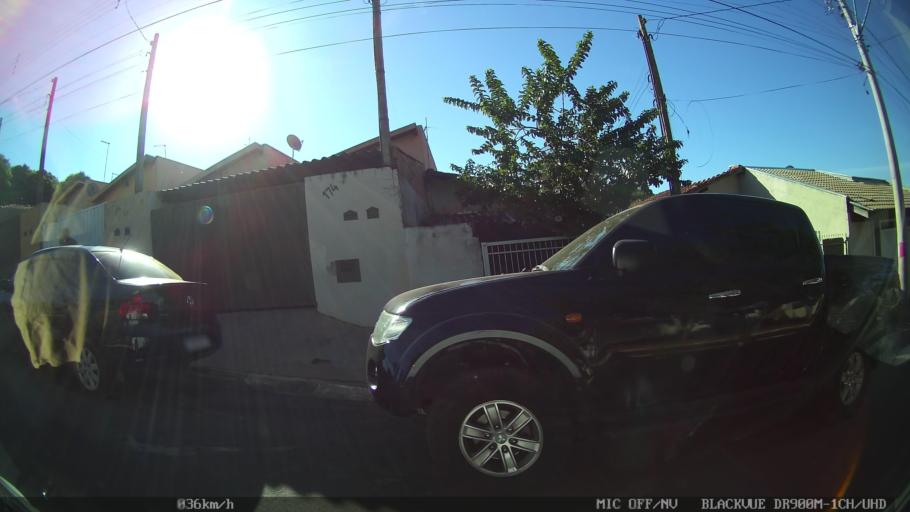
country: BR
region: Sao Paulo
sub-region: Olimpia
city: Olimpia
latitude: -20.7243
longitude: -48.8906
